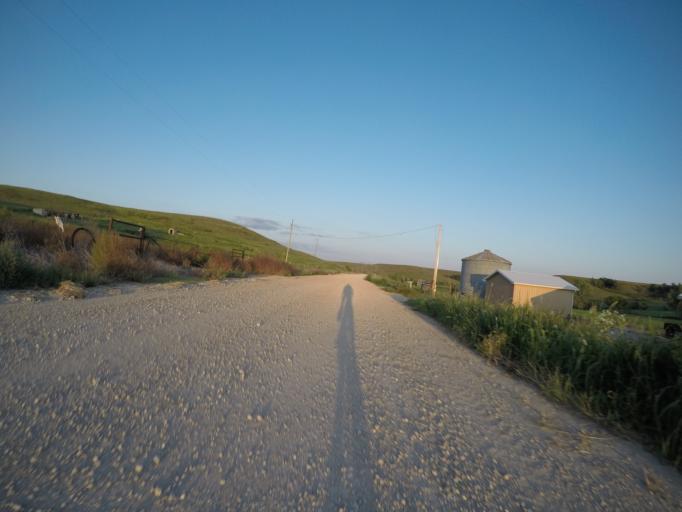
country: US
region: Kansas
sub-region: Riley County
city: Ogden
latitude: 39.0055
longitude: -96.6201
